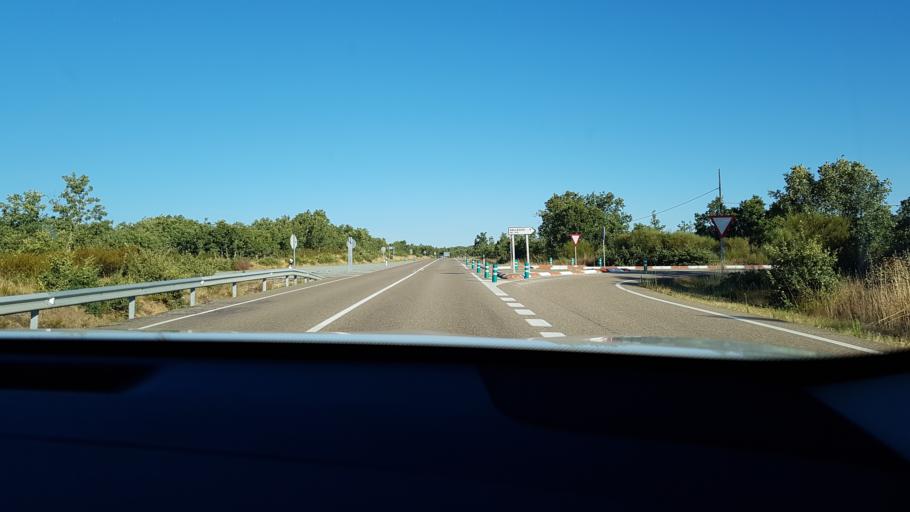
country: ES
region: Castille and Leon
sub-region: Provincia de Zamora
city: Samir de los Canos
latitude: 41.6689
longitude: -6.2259
